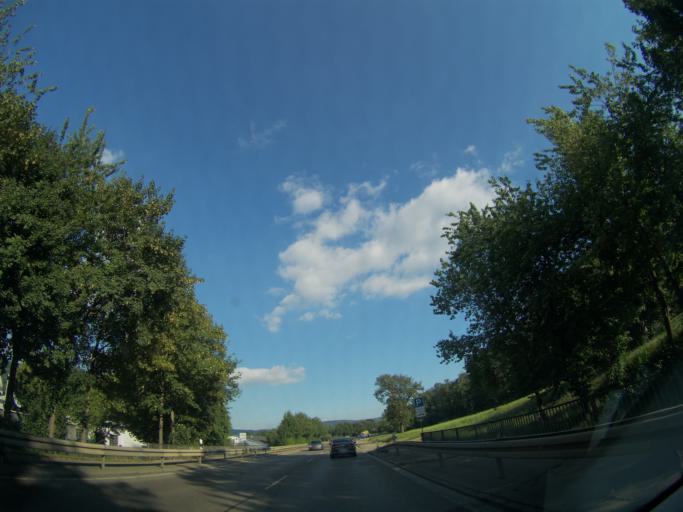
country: DE
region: Baden-Wuerttemberg
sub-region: Regierungsbezirk Stuttgart
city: Gingen an der Fils
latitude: 48.6470
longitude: 9.7872
